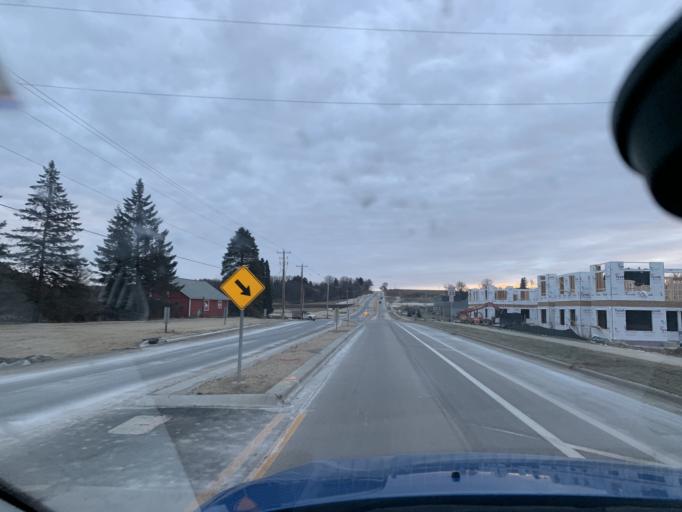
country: US
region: Wisconsin
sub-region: Dane County
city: Verona
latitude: 43.0522
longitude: -89.5523
